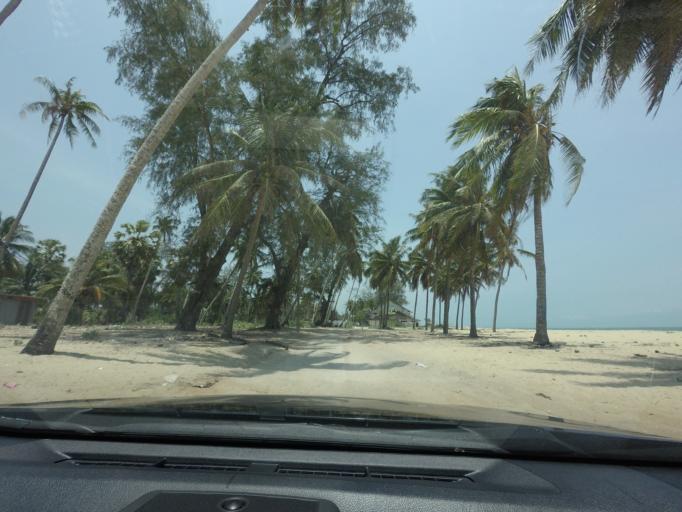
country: TH
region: Pattani
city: Yaring
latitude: 6.8980
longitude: 101.3748
